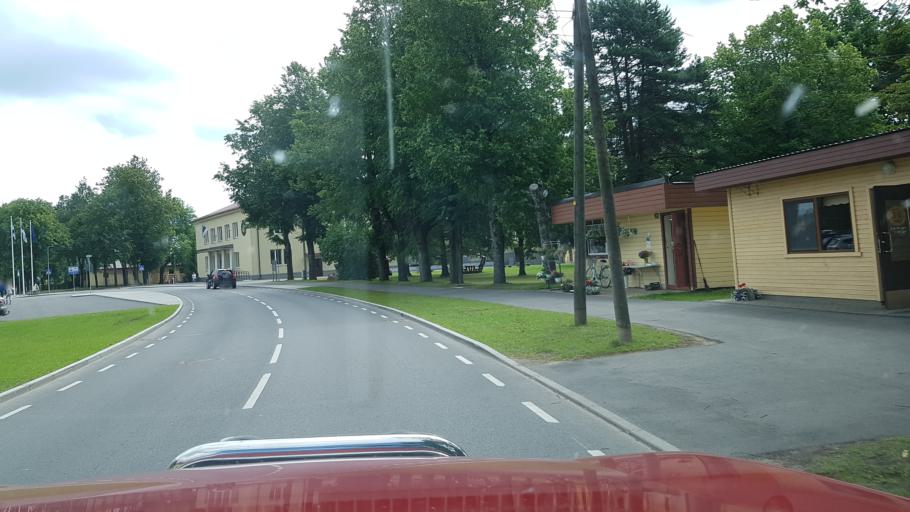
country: EE
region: Jogevamaa
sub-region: Mustvee linn
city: Mustvee
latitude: 58.8477
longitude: 26.9420
